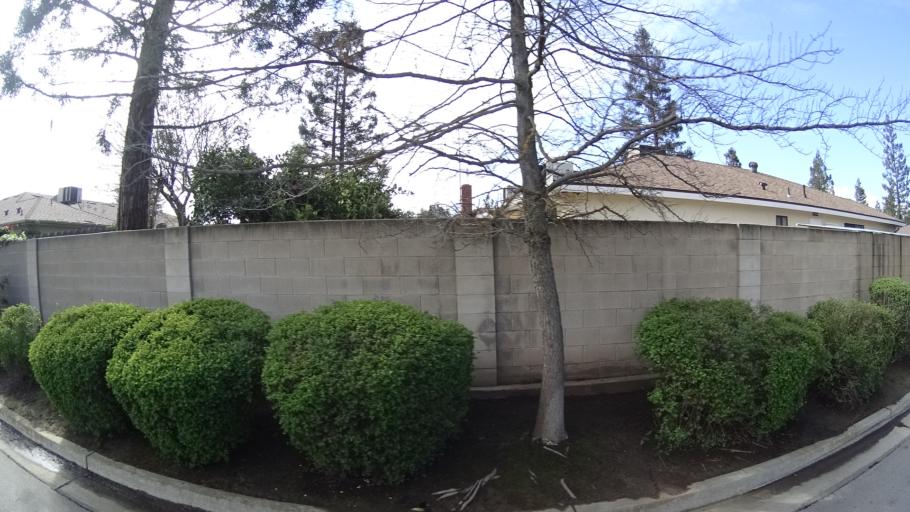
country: US
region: California
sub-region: Fresno County
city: Fresno
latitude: 36.8331
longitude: -119.8607
